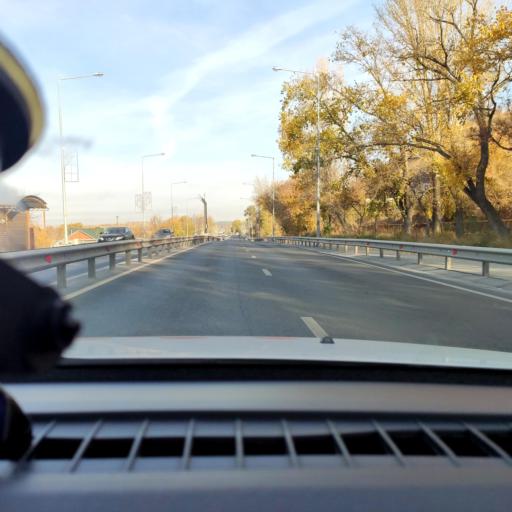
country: RU
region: Samara
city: Volzhskiy
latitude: 53.4042
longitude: 50.1461
